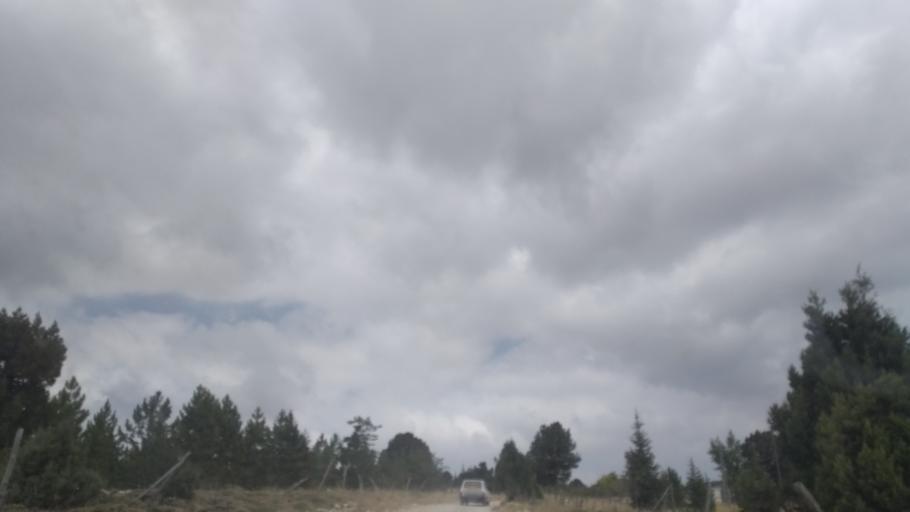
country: TR
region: Mersin
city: Sarikavak
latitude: 36.5700
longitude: 33.7641
